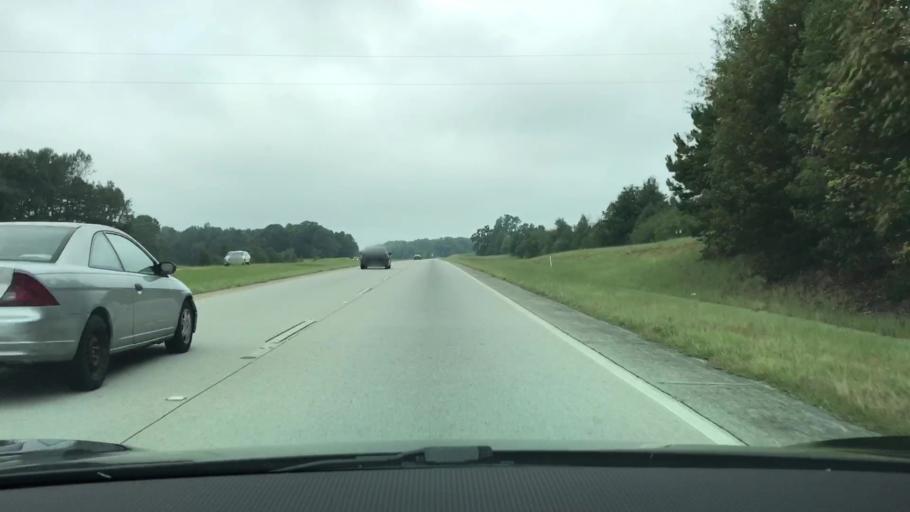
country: US
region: Georgia
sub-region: Oconee County
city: Bogart
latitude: 33.9399
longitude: -83.5532
